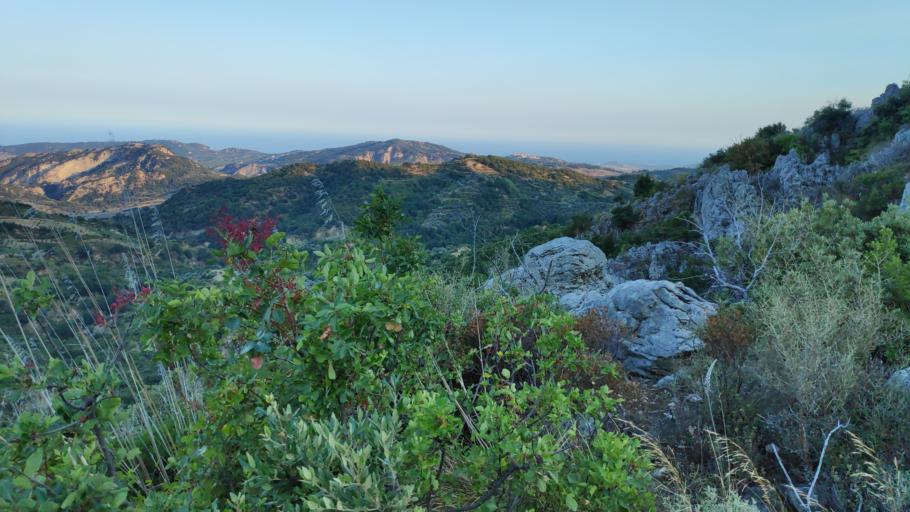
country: IT
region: Calabria
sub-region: Provincia di Reggio Calabria
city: Pazzano
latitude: 38.4624
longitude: 16.4468
